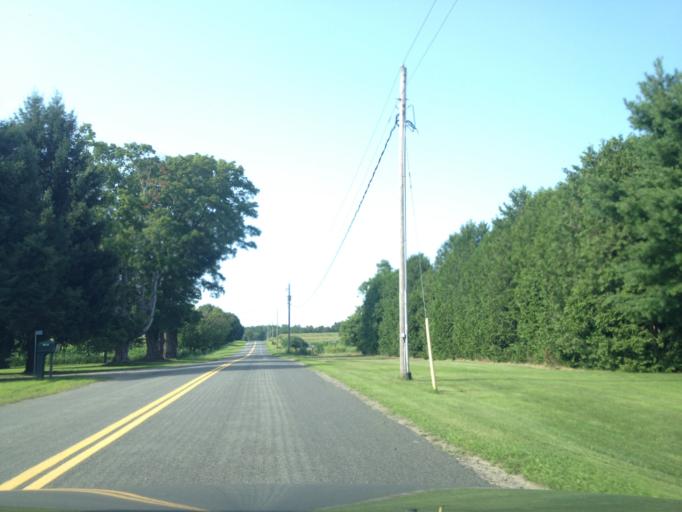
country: CA
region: Ontario
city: Aylmer
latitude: 42.7391
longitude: -80.8533
